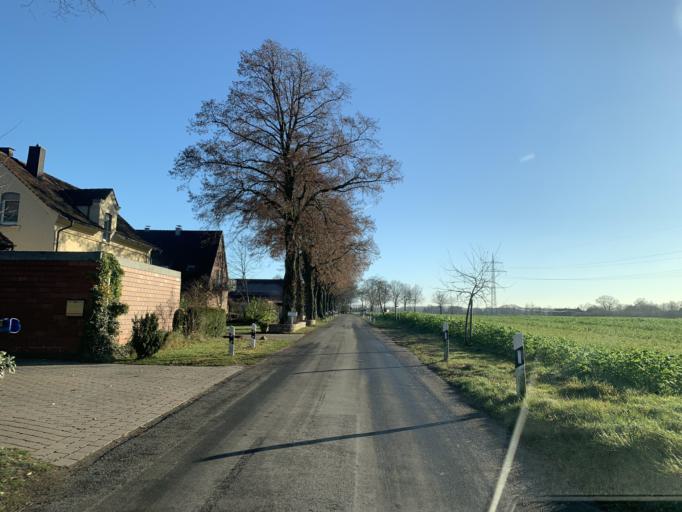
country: DE
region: North Rhine-Westphalia
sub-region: Regierungsbezirk Munster
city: Dulmen
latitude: 51.8651
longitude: 7.2930
